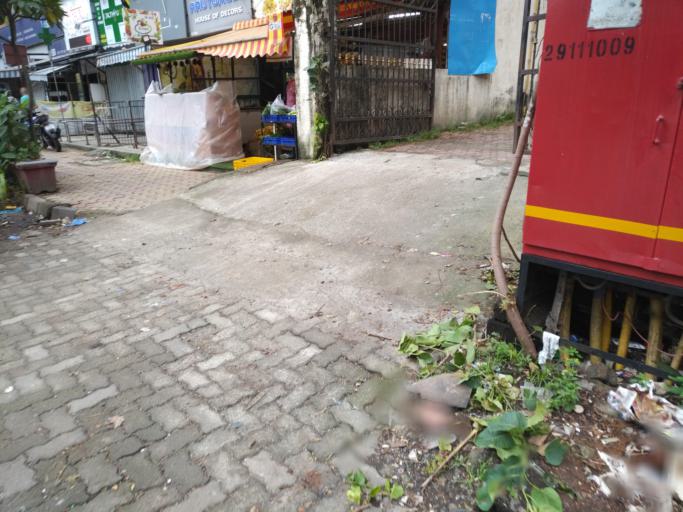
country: IN
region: Maharashtra
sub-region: Mumbai Suburban
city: Borivli
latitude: 19.2404
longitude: 72.8648
